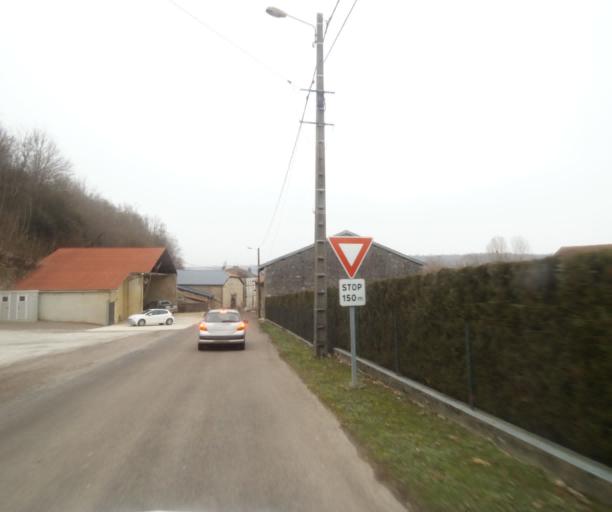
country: FR
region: Champagne-Ardenne
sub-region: Departement de la Haute-Marne
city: Bienville
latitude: 48.5479
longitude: 5.0719
